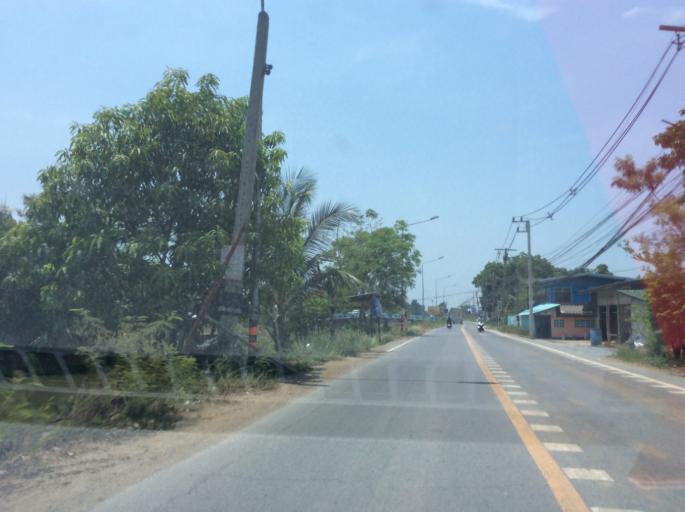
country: TH
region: Pathum Thani
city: Ban Rangsit
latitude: 14.0202
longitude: 100.7783
